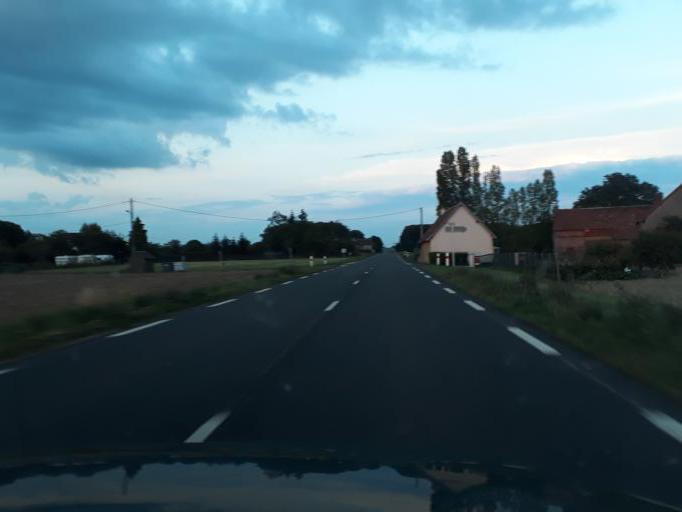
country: FR
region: Centre
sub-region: Departement du Loir-et-Cher
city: La Ville-aux-Clercs
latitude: 47.8918
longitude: 1.0632
